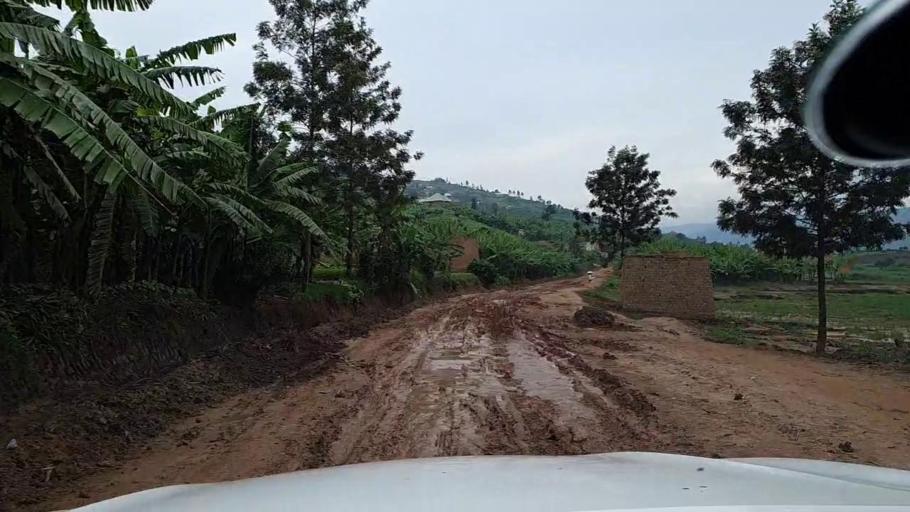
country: RW
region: Kigali
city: Kigali
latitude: -1.9489
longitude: 29.9899
